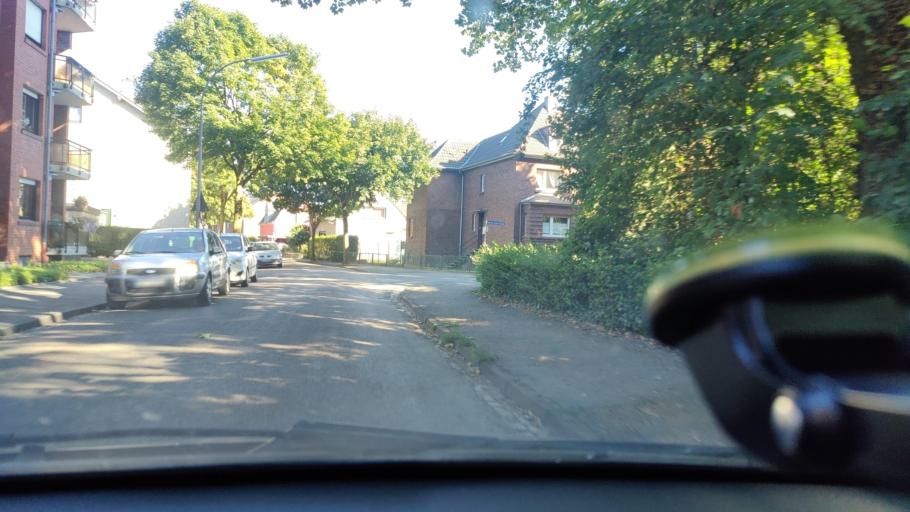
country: DE
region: North Rhine-Westphalia
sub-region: Regierungsbezirk Dusseldorf
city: Kleve
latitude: 51.7958
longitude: 6.1591
